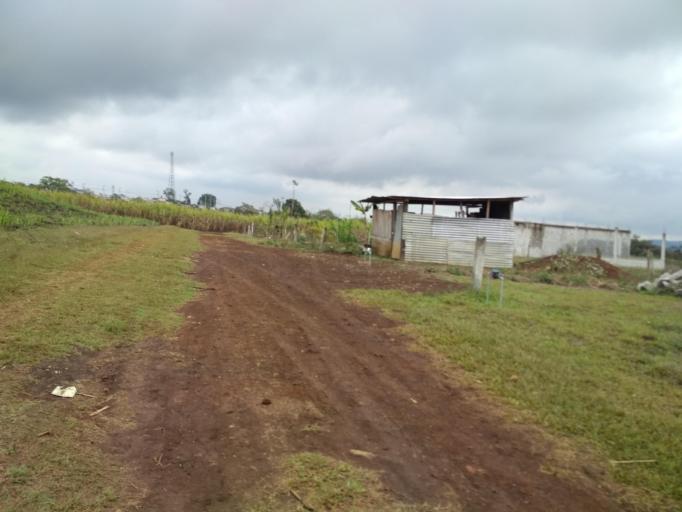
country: MX
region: Veracruz
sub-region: Cordoba
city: San Jose de Tapia
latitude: 18.8505
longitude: -96.9632
